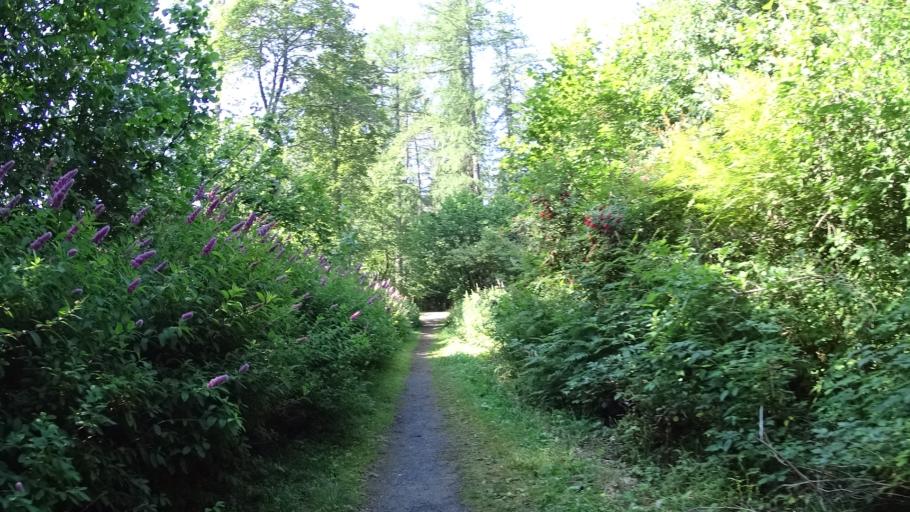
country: FI
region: Haeme
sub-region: Haemeenlinna
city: Haemeenlinna
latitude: 61.0235
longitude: 24.4531
